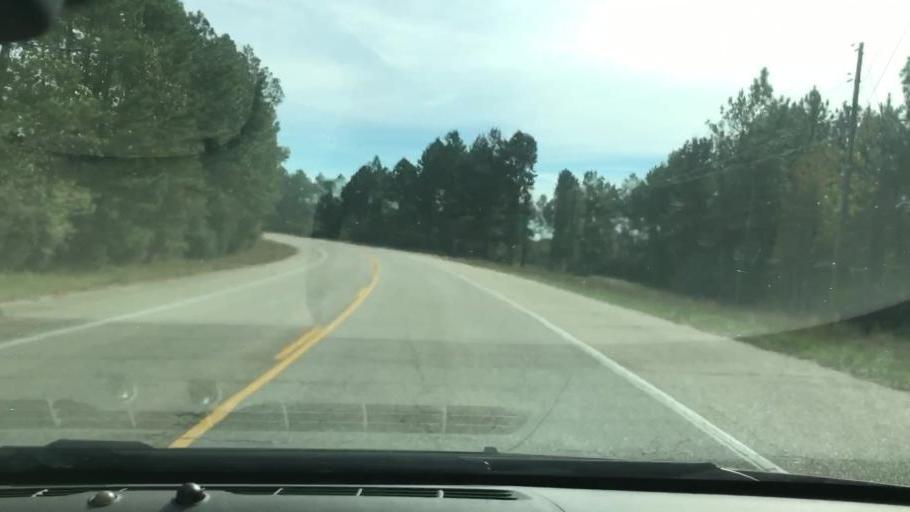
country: US
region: Mississippi
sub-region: Pearl River County
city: Nicholson
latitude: 30.5246
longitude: -89.8554
